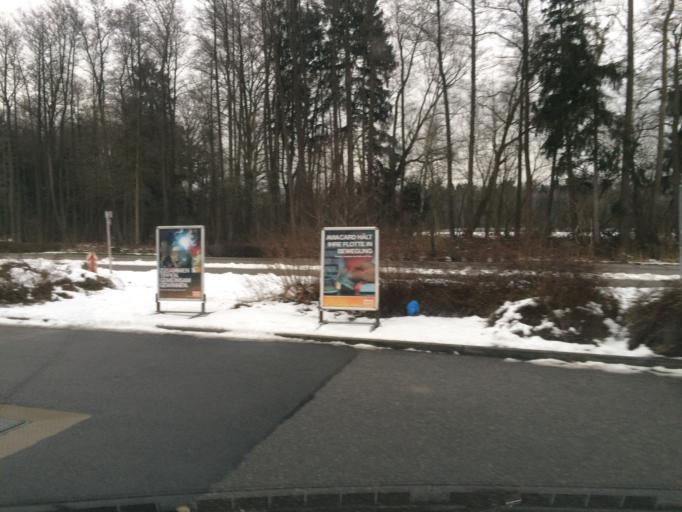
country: DE
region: Bavaria
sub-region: Upper Palatinate
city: Teublitz
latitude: 49.2222
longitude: 12.0956
